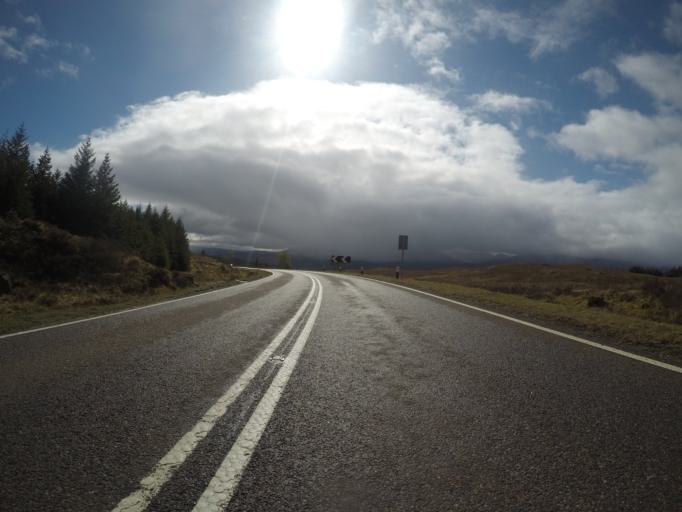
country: GB
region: Scotland
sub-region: Highland
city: Spean Bridge
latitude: 57.0945
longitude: -4.9937
